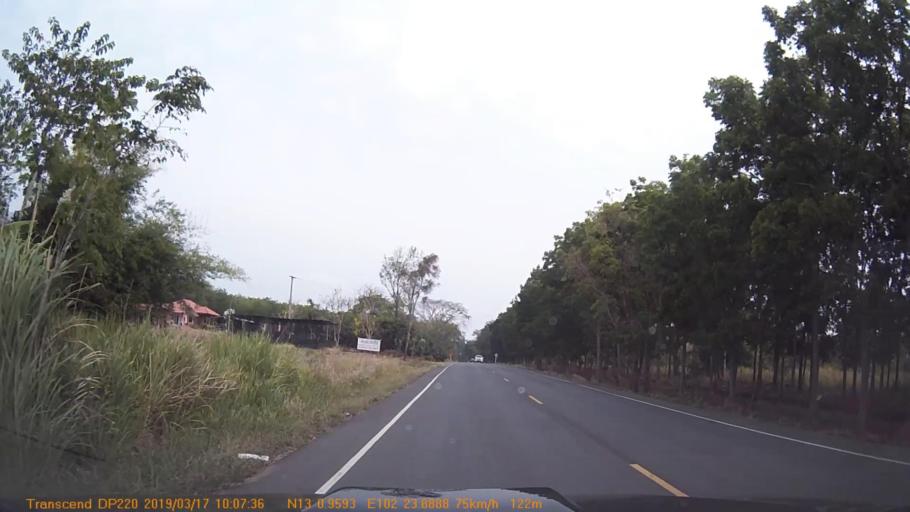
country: TH
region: Chanthaburi
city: Pong Nam Ron
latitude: 13.0185
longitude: 102.3982
